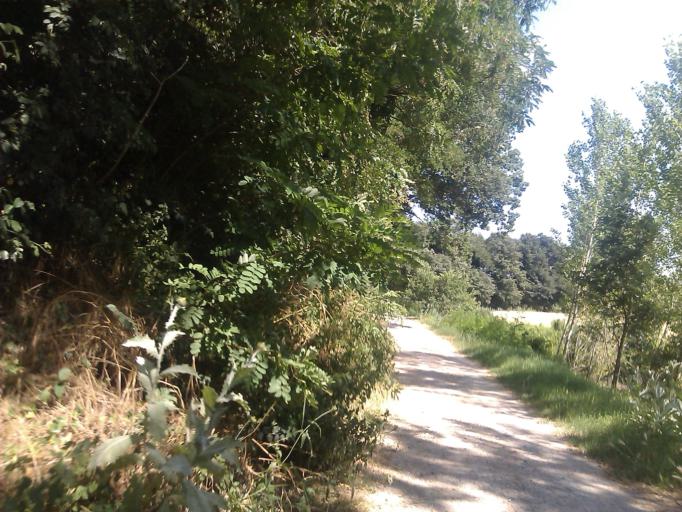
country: IT
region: Tuscany
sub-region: Provincia di Siena
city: Chiusi
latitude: 43.0562
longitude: 11.9366
